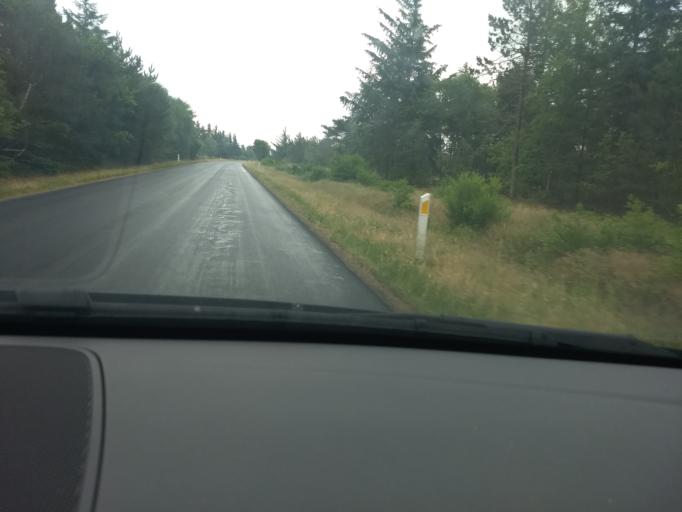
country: DK
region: South Denmark
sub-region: Fano Kommune
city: Nordby
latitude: 55.3775
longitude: 8.4477
